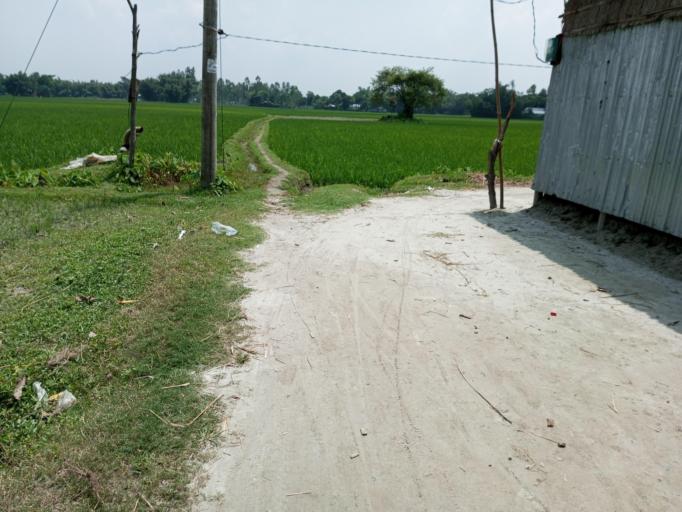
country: BD
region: Rangpur Division
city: Rangpur
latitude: 25.9061
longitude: 89.2710
